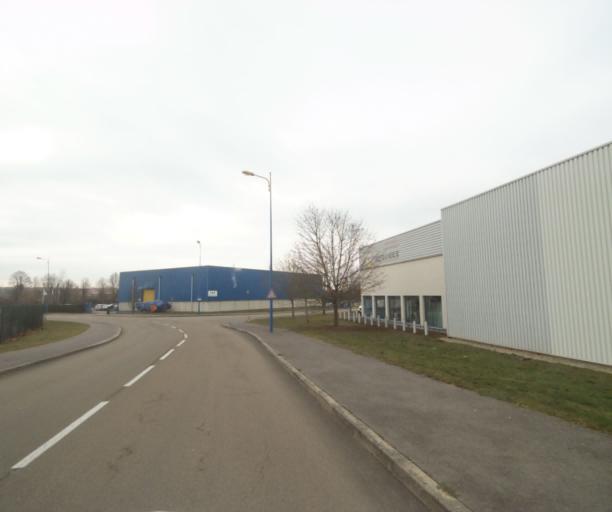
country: FR
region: Champagne-Ardenne
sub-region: Departement de la Haute-Marne
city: Bettancourt-la-Ferree
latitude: 48.6350
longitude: 4.9792
